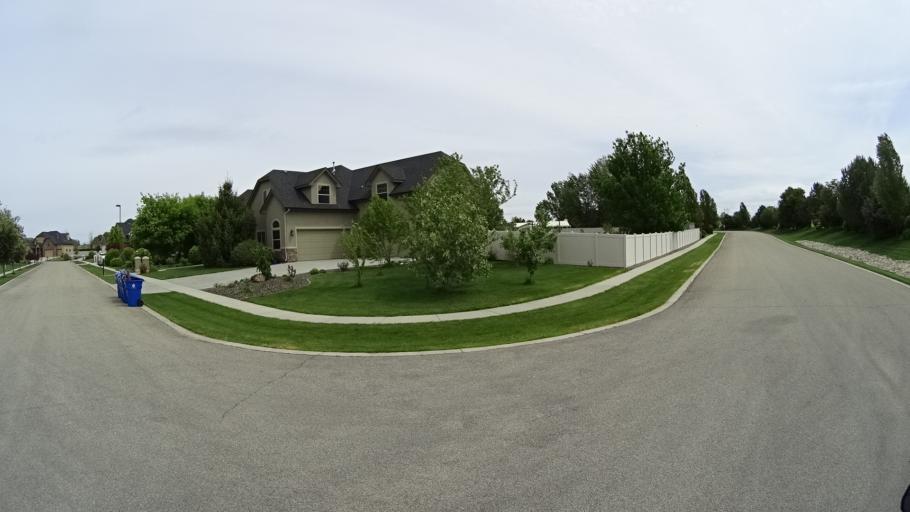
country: US
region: Idaho
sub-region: Ada County
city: Kuna
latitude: 43.5383
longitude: -116.4009
